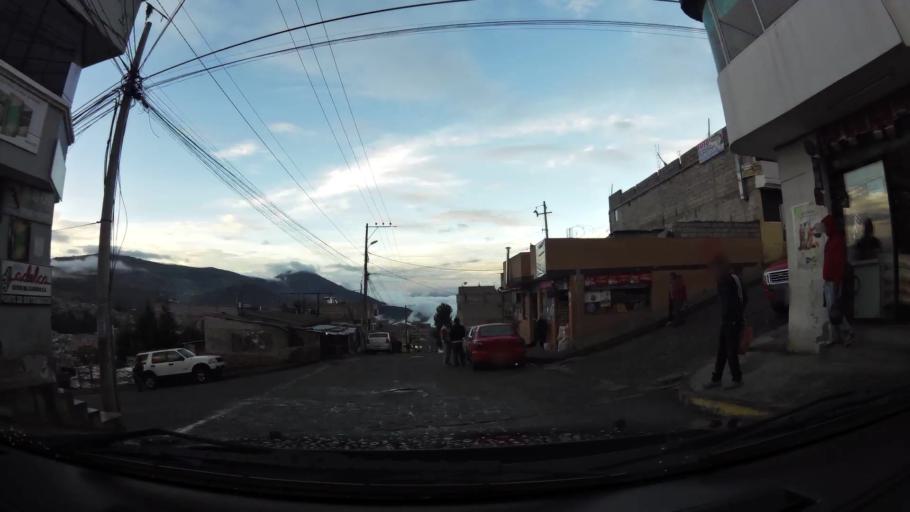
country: EC
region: Pichincha
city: Quito
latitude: -0.0991
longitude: -78.5203
